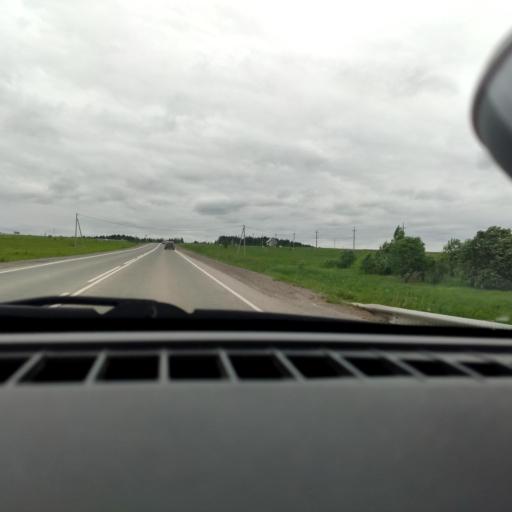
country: RU
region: Perm
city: Kultayevo
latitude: 57.8969
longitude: 55.7903
